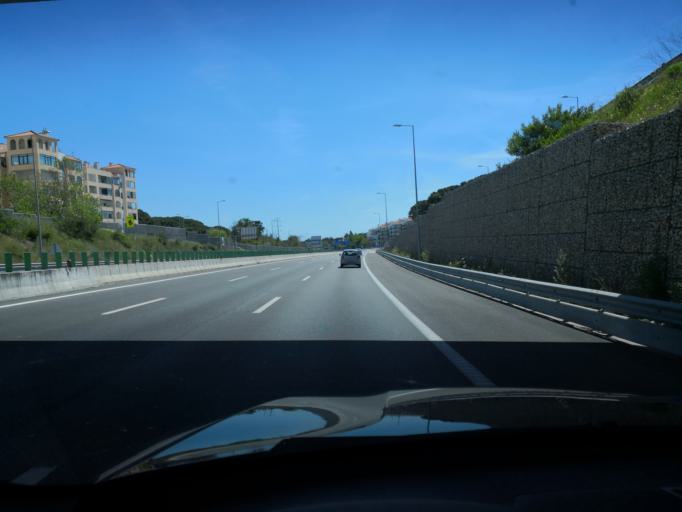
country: PT
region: Setubal
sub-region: Almada
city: Sobreda
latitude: 38.6471
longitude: -9.2010
